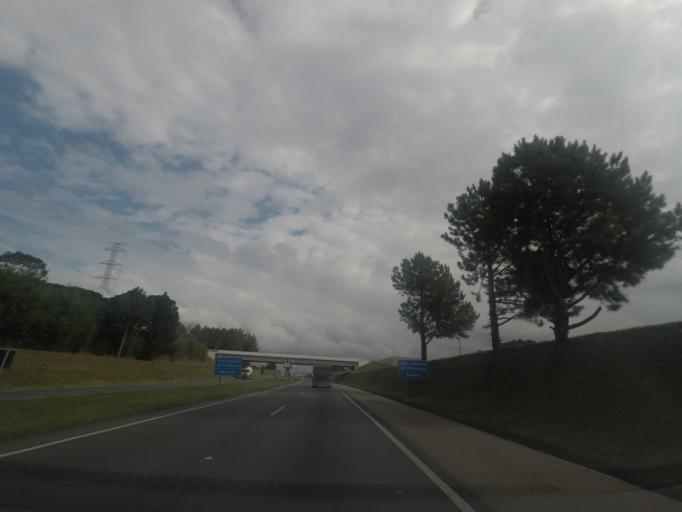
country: BR
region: Parana
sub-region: Piraquara
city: Piraquara
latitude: -25.4845
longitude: -49.1082
